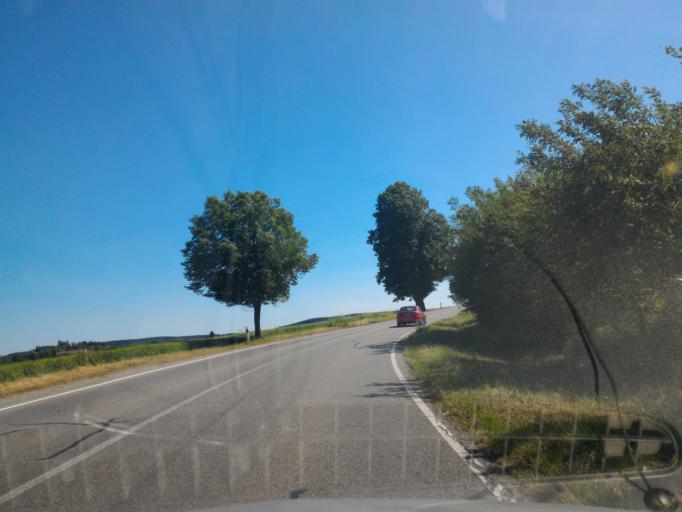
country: CZ
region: Vysocina
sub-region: Okres Jihlava
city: Trest'
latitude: 49.2796
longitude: 15.4772
